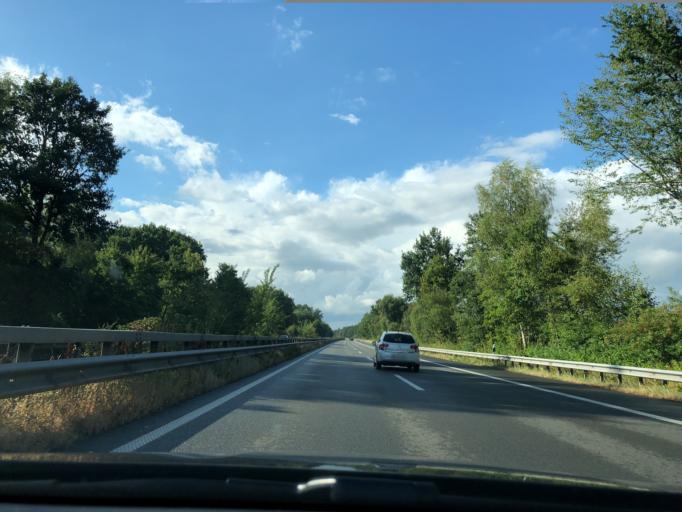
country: DE
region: Lower Saxony
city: Bad Zwischenahn
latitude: 53.2307
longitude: 8.0334
